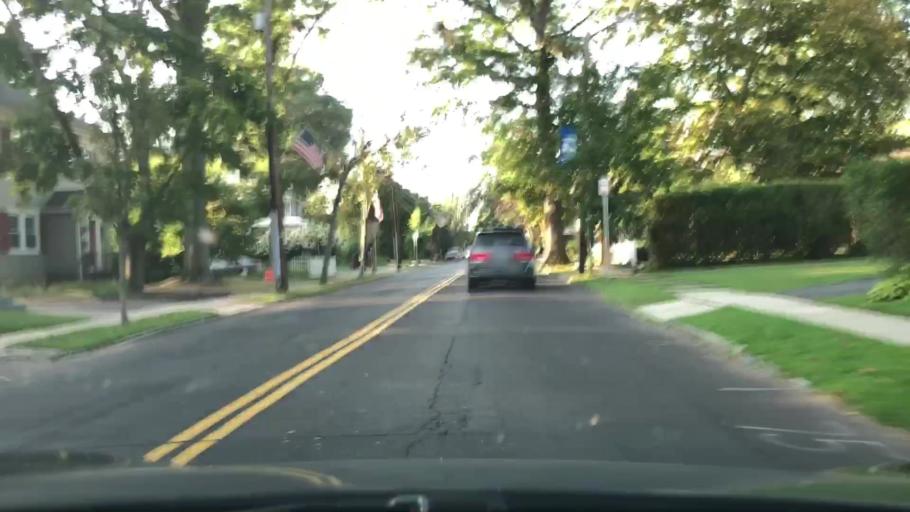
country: US
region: New Jersey
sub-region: Mercer County
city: Pennington
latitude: 40.3232
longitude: -74.7905
